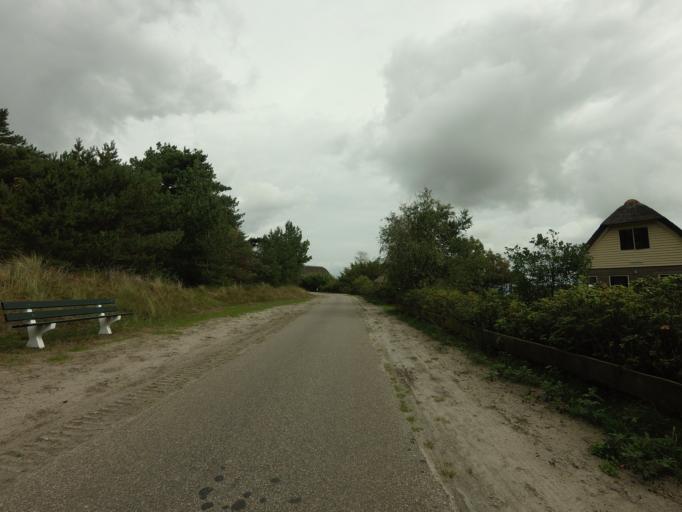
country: NL
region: Friesland
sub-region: Gemeente Ameland
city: Hollum
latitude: 53.4458
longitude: 5.6258
